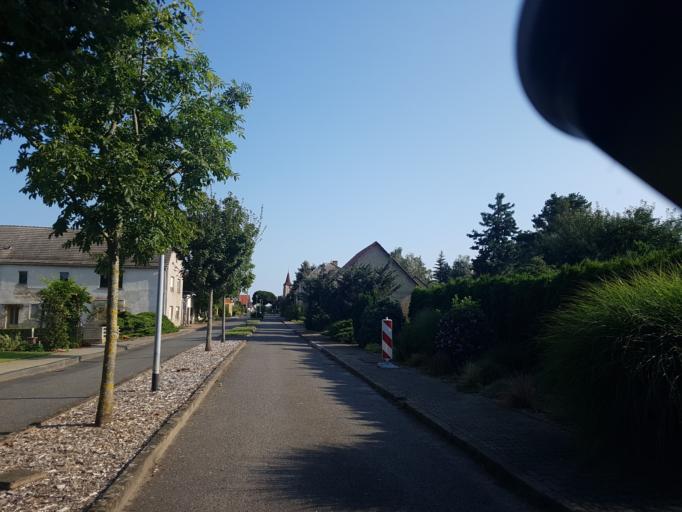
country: DE
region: Brandenburg
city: Niemegk
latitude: 52.1251
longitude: 12.7040
